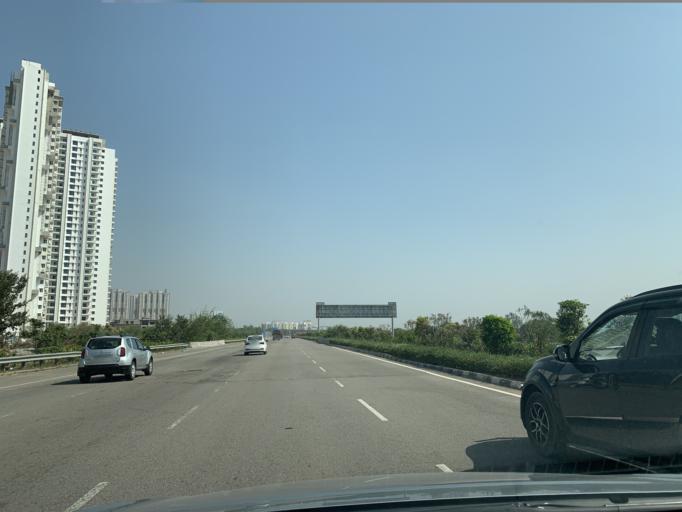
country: IN
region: Telangana
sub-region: Medak
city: Serilingampalle
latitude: 17.4007
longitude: 78.3435
